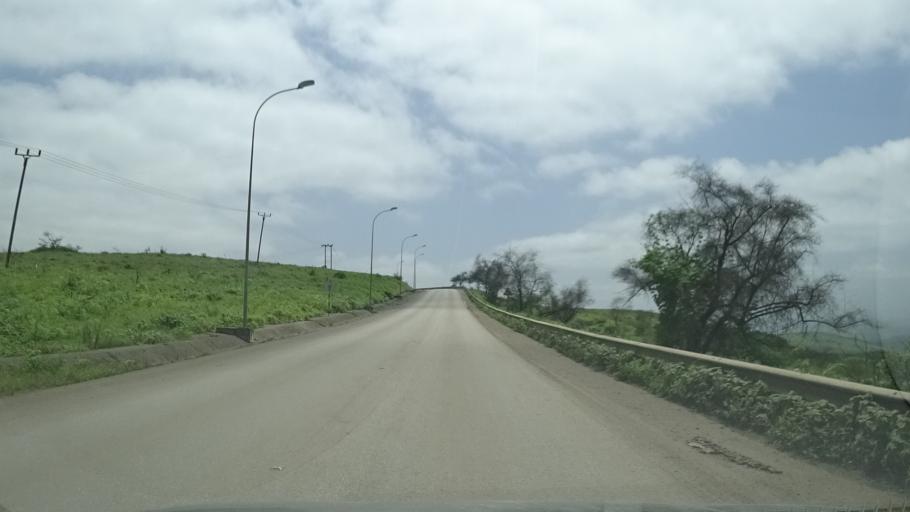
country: OM
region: Zufar
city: Salalah
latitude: 17.1663
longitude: 54.2228
